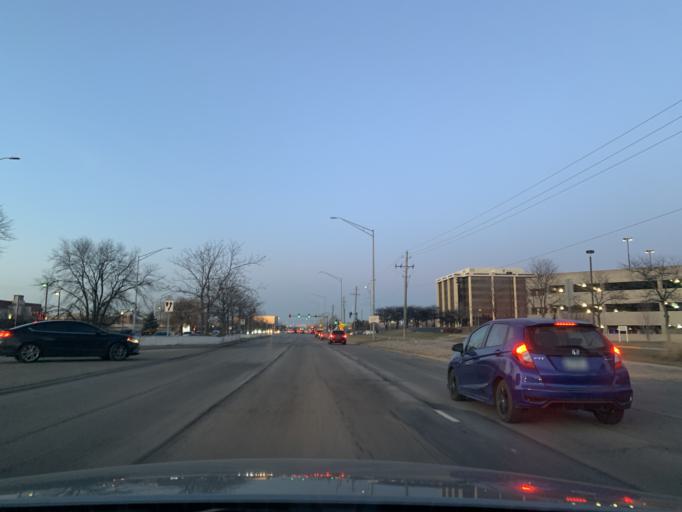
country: US
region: Illinois
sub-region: Cook County
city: Hoffman Estates
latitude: 42.0460
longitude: -88.0452
